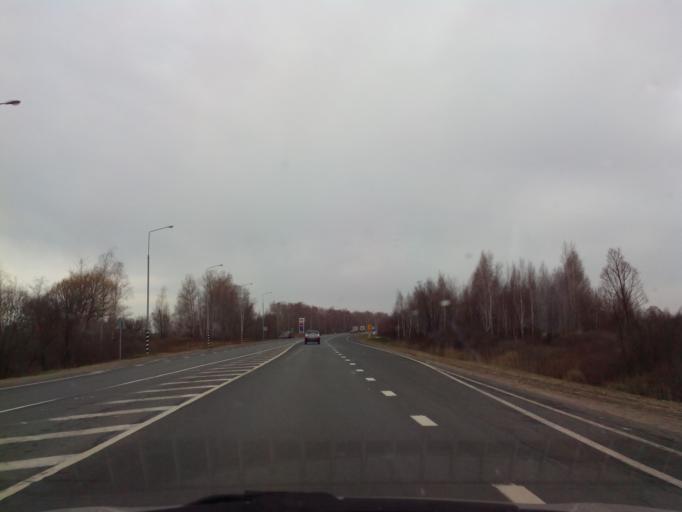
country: RU
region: Tambov
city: Pervomayskiy
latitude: 53.0848
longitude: 40.4053
